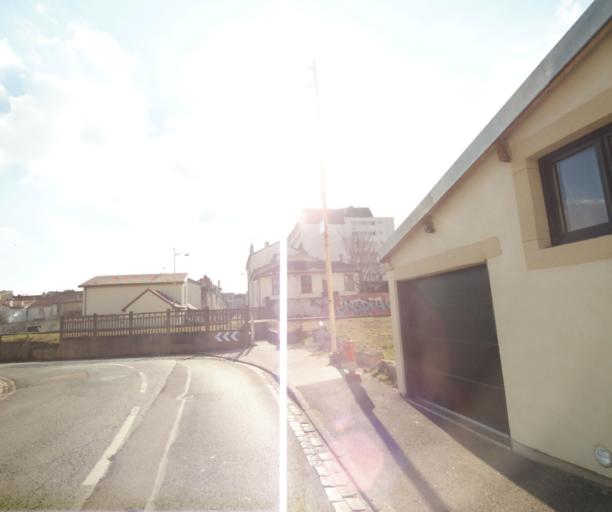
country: FR
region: Lorraine
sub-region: Departement de Meurthe-et-Moselle
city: Malzeville
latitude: 48.7008
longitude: 6.1916
